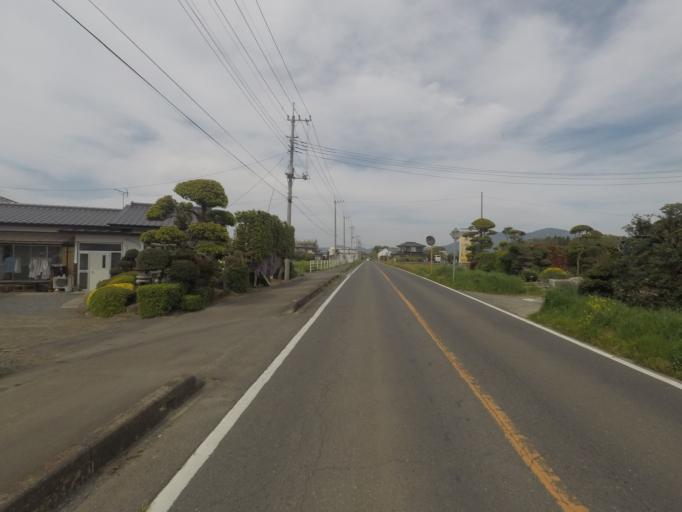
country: JP
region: Ibaraki
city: Makabe
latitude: 36.2694
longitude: 140.0681
